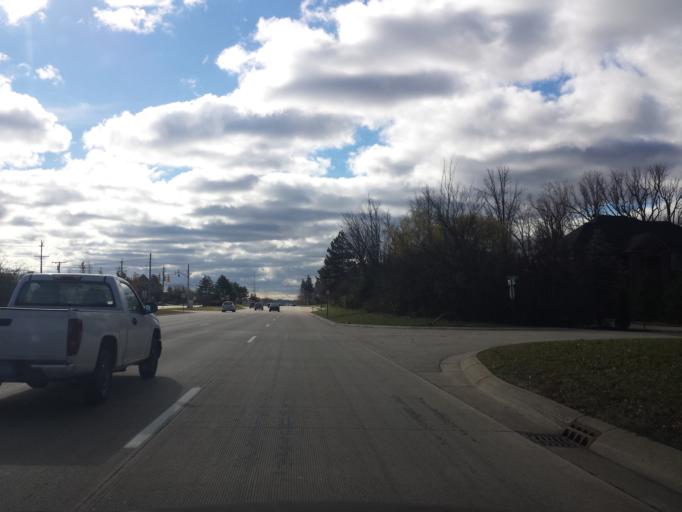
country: US
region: Michigan
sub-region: Oakland County
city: Bingham Farms
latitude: 42.5094
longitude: -83.2858
